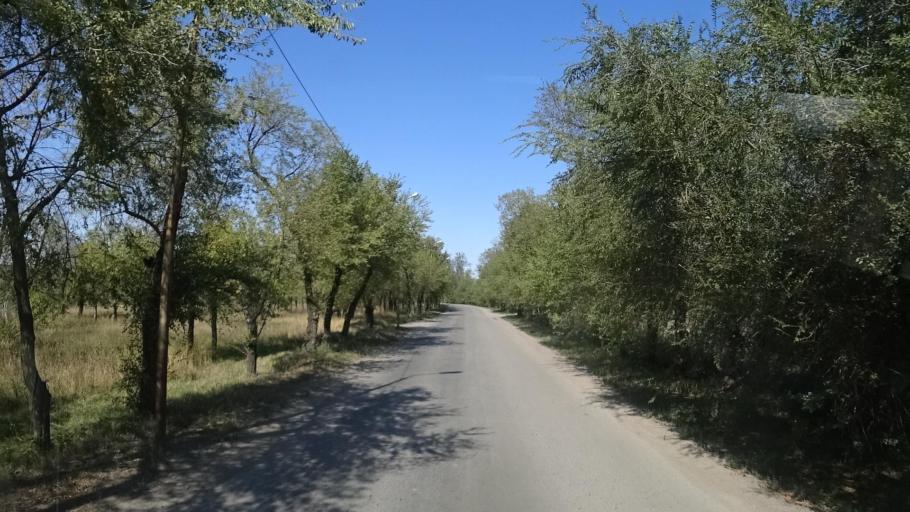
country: KZ
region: Almaty Oblysy
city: Pervomayskiy
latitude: 43.3316
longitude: 77.0015
